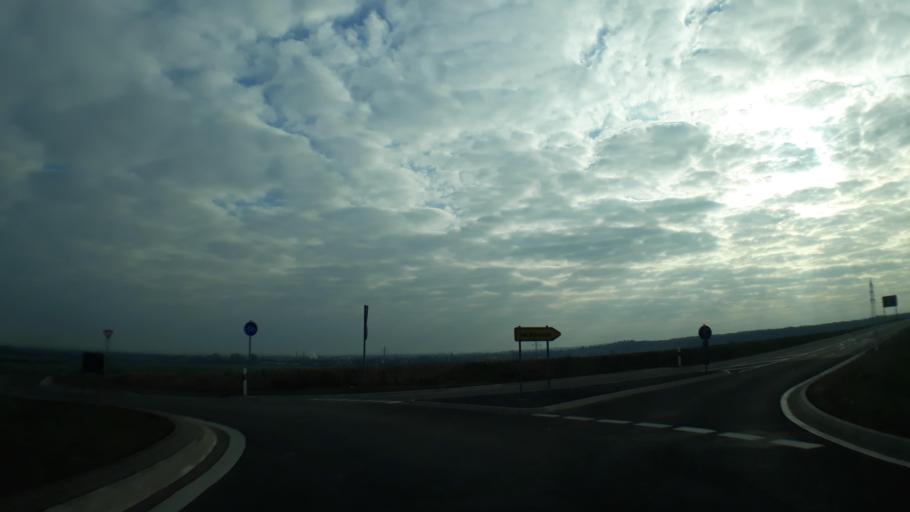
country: DE
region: North Rhine-Westphalia
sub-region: Regierungsbezirk Koln
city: Euskirchen
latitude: 50.6265
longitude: 6.7812
